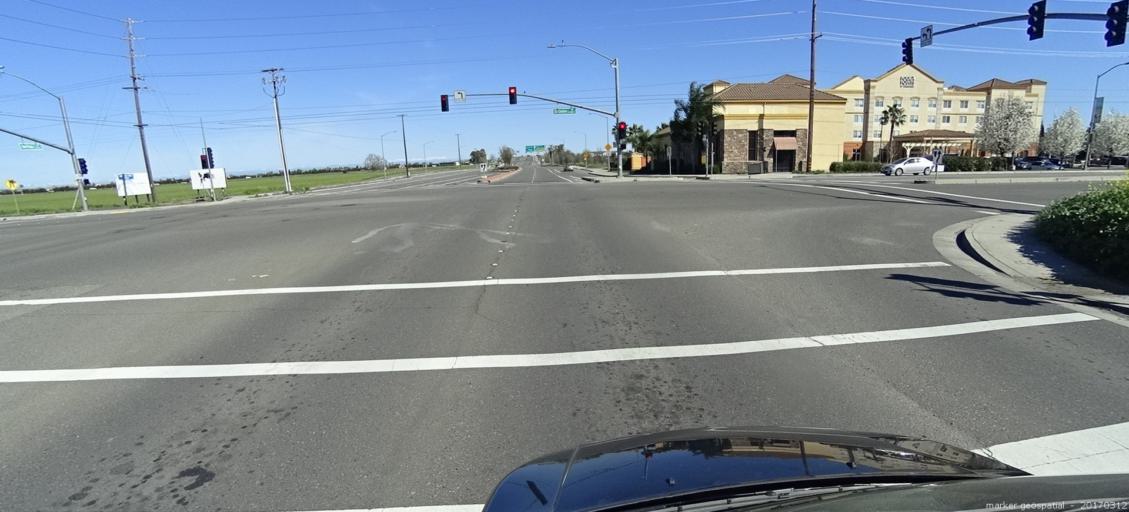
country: US
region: California
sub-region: Yolo County
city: West Sacramento
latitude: 38.6556
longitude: -121.5402
